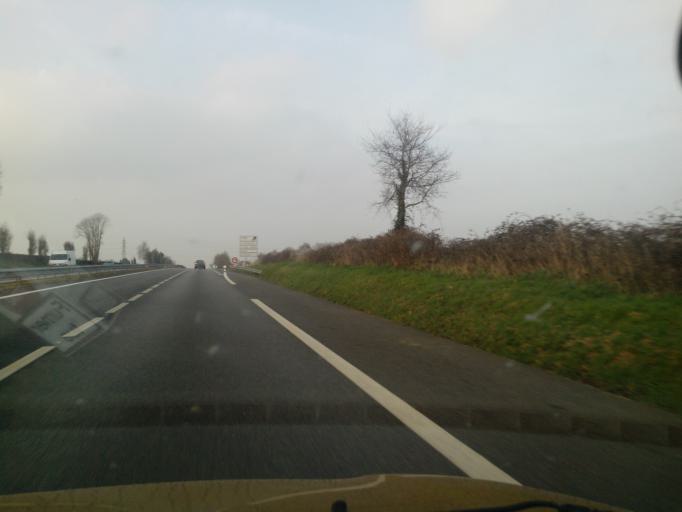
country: FR
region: Brittany
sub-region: Departement du Morbihan
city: Ploermel
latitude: 47.9036
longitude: -2.4109
